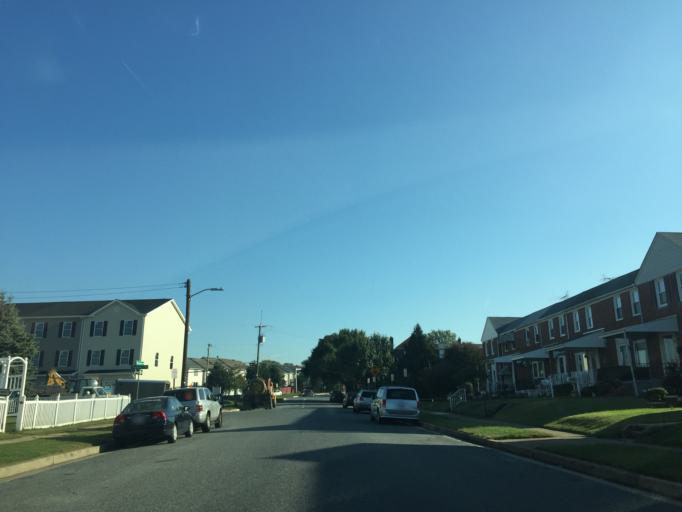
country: US
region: Maryland
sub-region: Baltimore County
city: Dundalk
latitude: 39.2808
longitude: -76.5294
